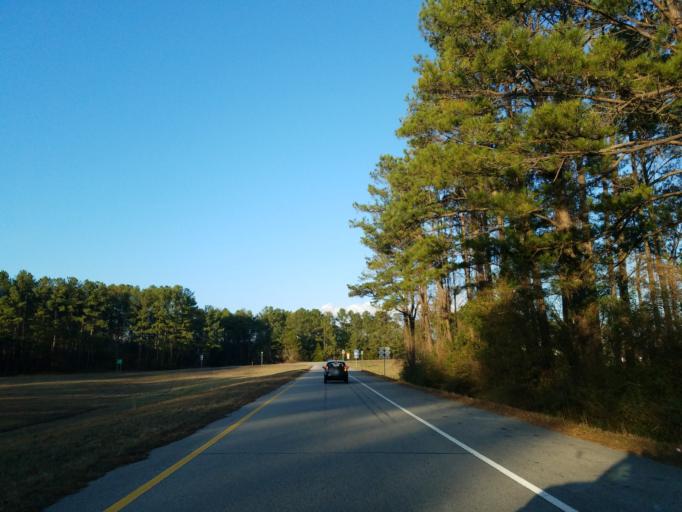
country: US
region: Mississippi
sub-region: Clarke County
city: Stonewall
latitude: 32.1624
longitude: -88.8665
